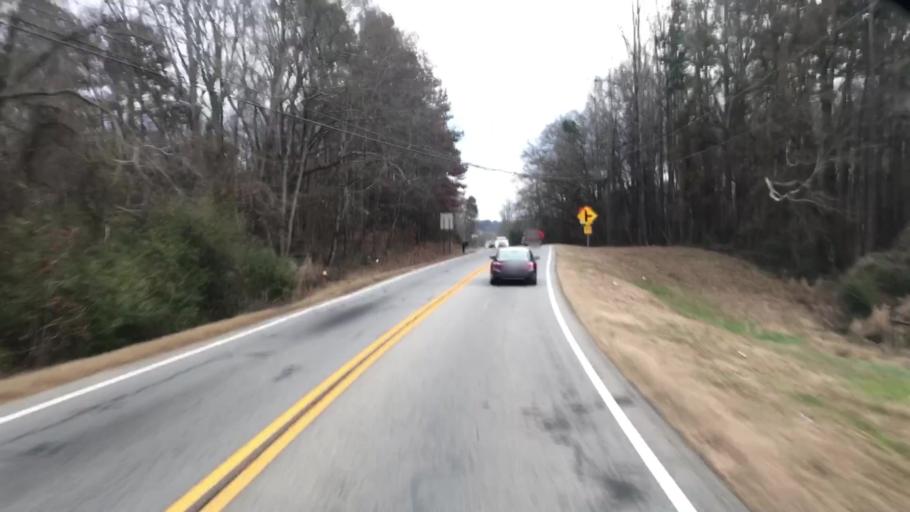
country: US
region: Georgia
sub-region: Barrow County
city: Winder
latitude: 34.0194
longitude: -83.7616
